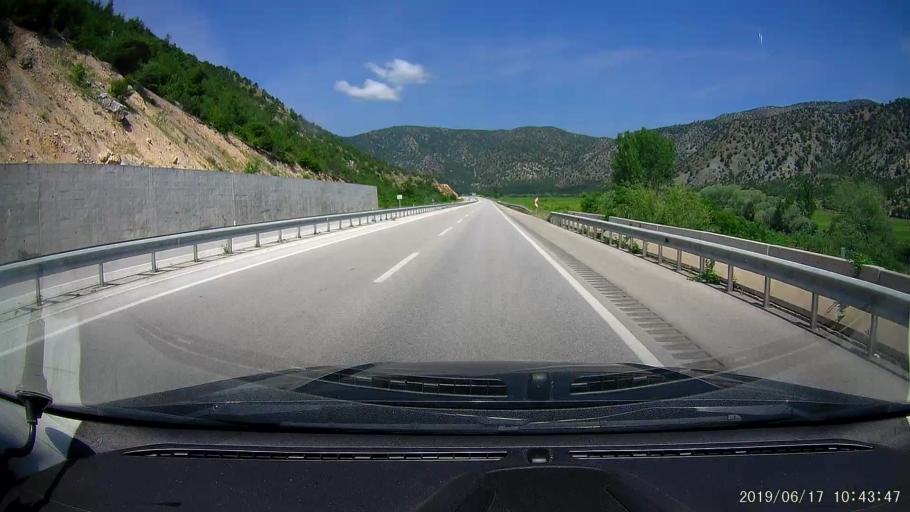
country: TR
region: Corum
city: Kargi
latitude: 41.0688
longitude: 34.5279
